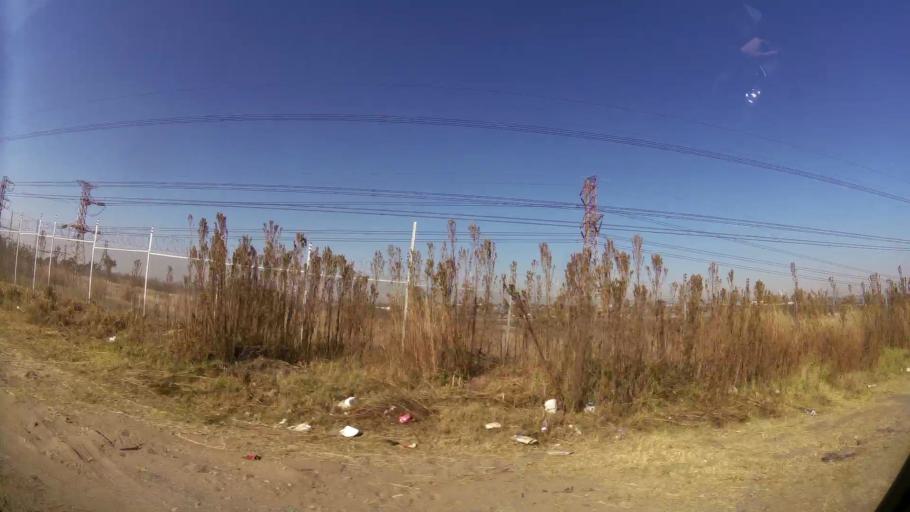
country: ZA
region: Gauteng
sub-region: Ekurhuleni Metropolitan Municipality
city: Germiston
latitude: -26.2289
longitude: 28.1120
